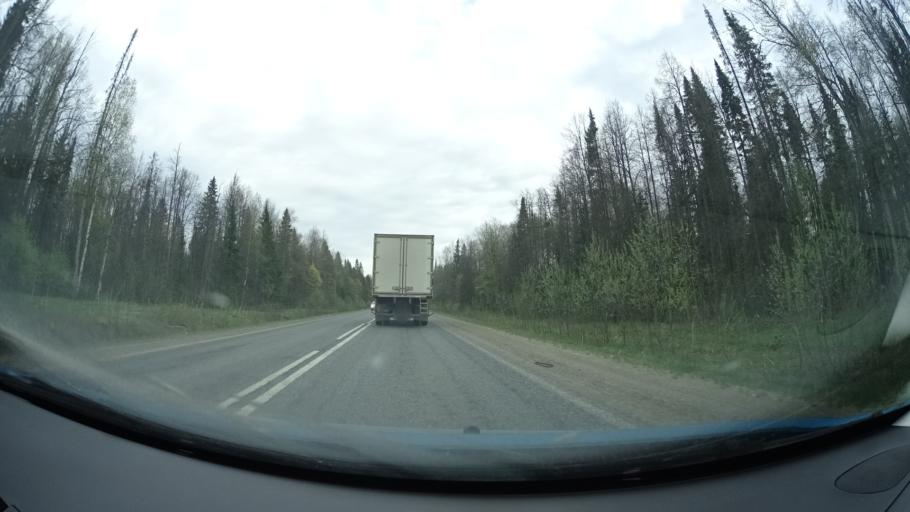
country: RU
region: Perm
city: Yugo-Kamskiy
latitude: 57.5881
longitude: 55.6703
